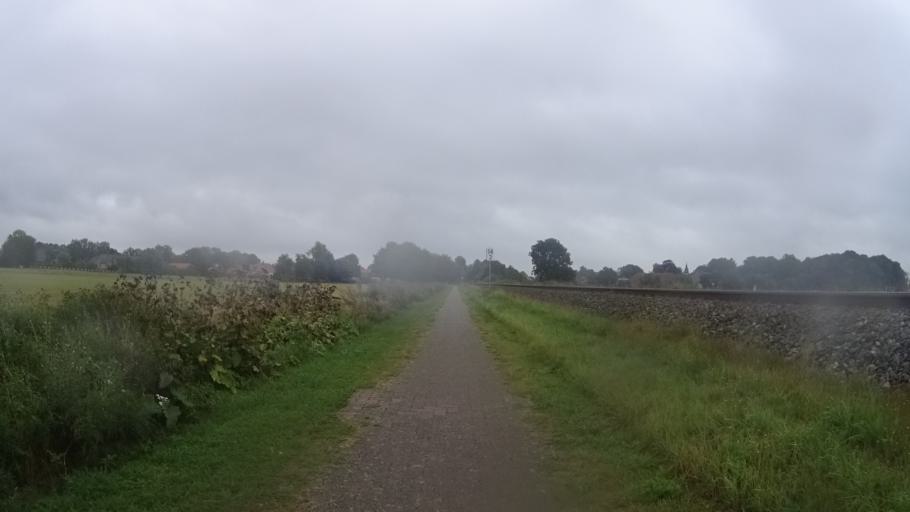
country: DE
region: Lower Saxony
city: Bunde
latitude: 53.1857
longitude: 7.2570
